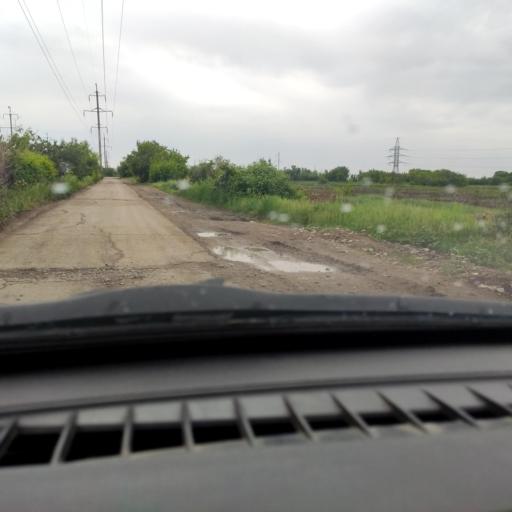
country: RU
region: Samara
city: Tol'yatti
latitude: 53.5887
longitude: 49.4356
